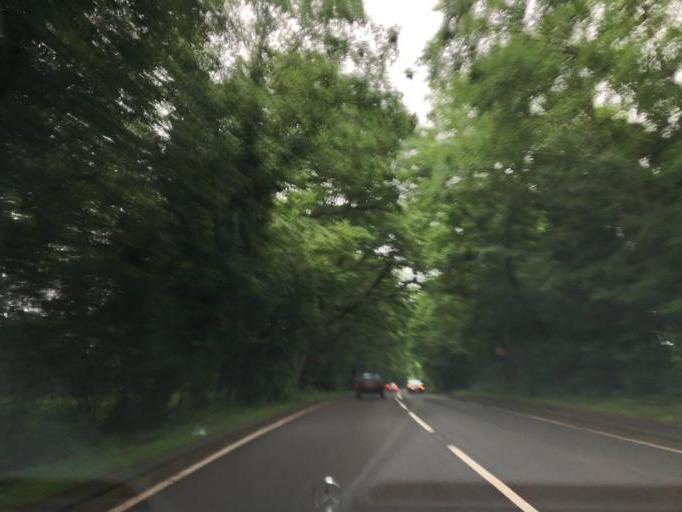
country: GB
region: England
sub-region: Warwickshire
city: Wroxall
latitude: 52.3181
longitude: -1.6668
